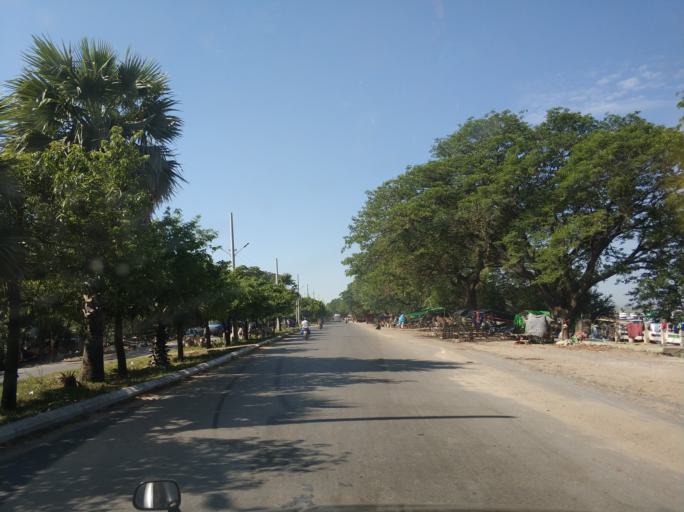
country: MM
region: Mandalay
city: Mandalay
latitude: 21.9674
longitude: 96.0562
